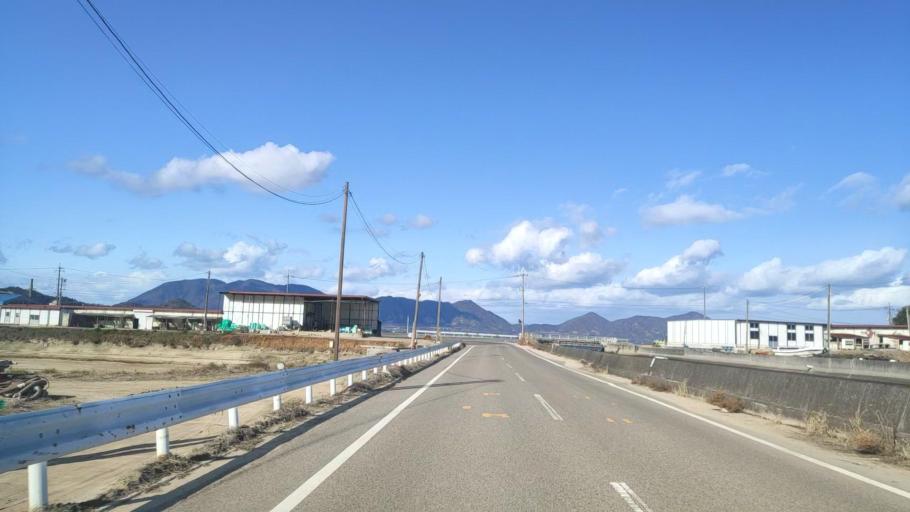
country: JP
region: Hiroshima
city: Innoshima
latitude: 34.2148
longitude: 133.1217
